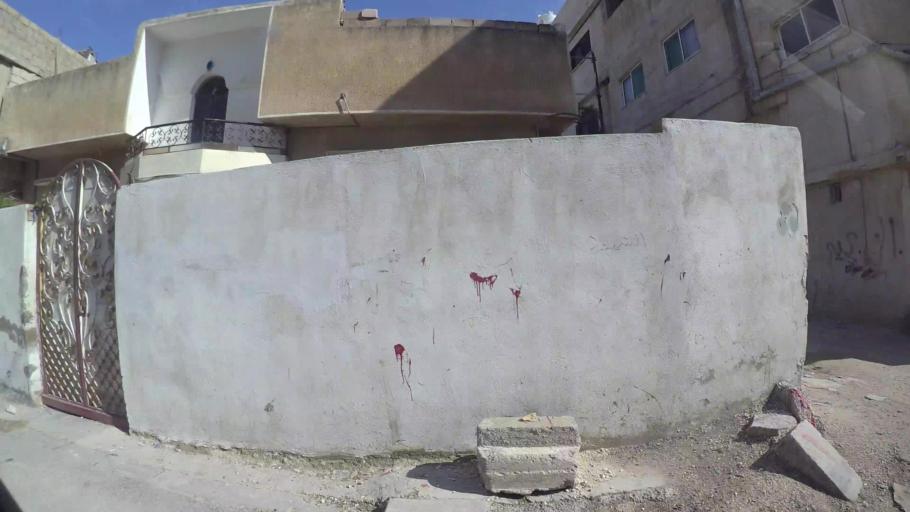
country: JO
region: Amman
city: Al Jubayhah
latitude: 32.0771
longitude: 35.8470
